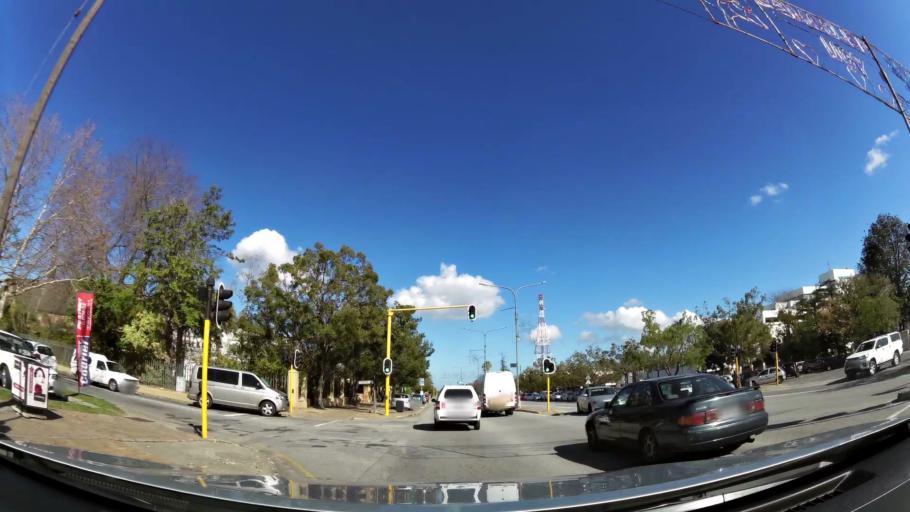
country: ZA
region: Western Cape
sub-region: Eden District Municipality
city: George
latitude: -33.9571
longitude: 22.4582
